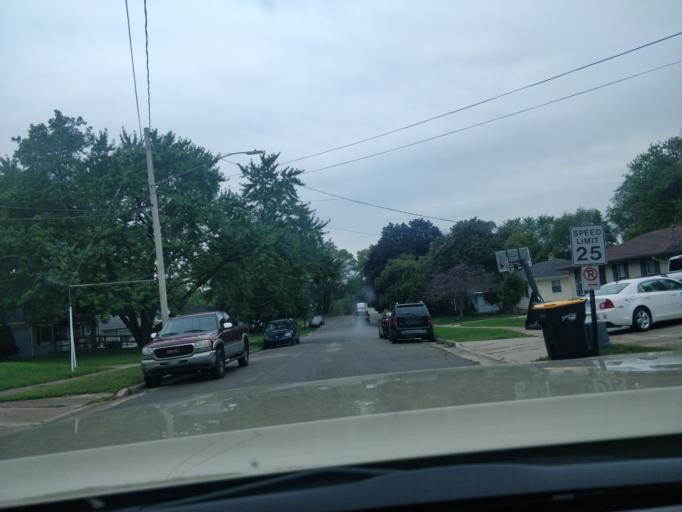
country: US
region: Michigan
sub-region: Kent County
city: Wyoming
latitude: 42.9176
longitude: -85.7253
